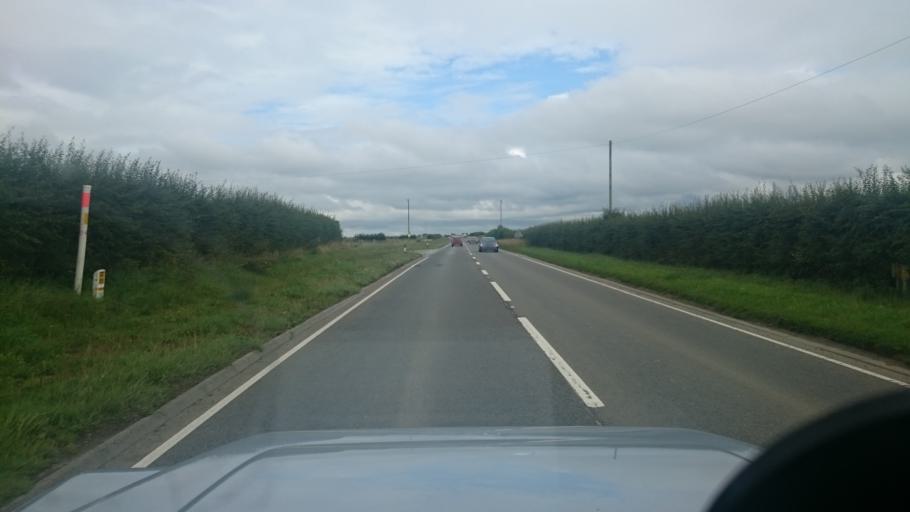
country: GB
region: Wales
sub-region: Pembrokeshire
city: Hook
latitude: 51.8058
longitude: -4.9277
